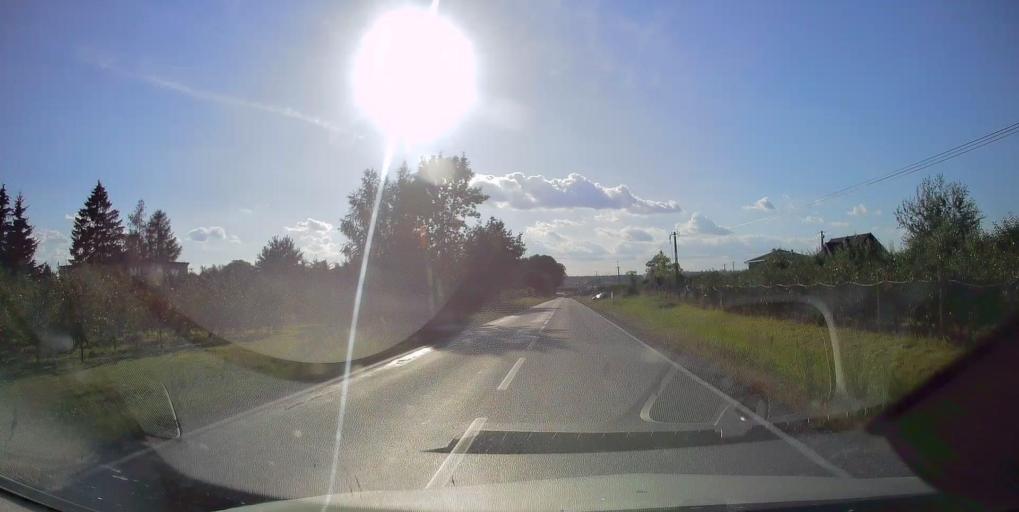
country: PL
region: Masovian Voivodeship
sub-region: Powiat grojecki
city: Bledow
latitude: 51.8135
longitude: 20.7465
